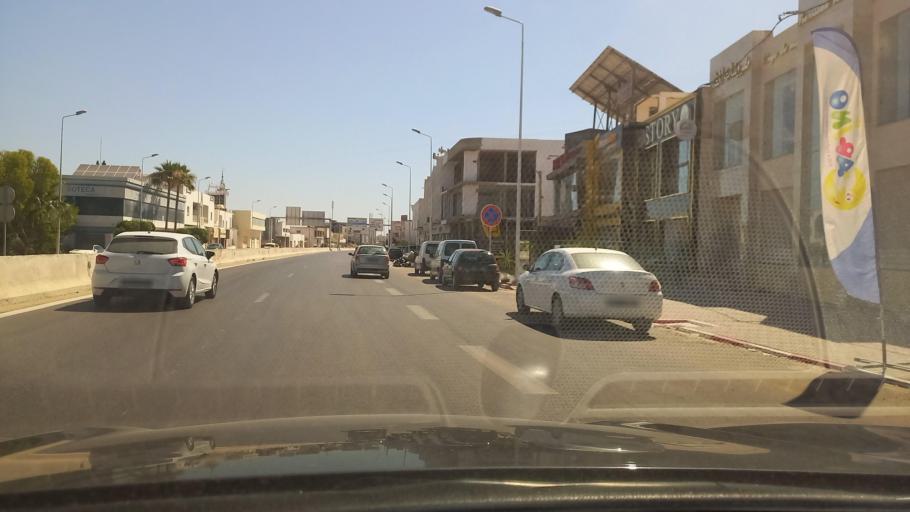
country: TN
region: Safaqis
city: Sfax
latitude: 34.7672
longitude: 10.7468
